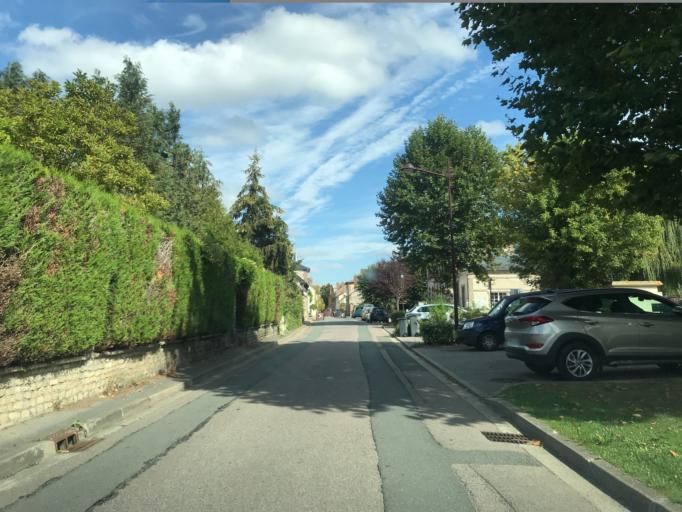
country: FR
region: Haute-Normandie
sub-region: Departement de l'Eure
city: Le Vaudreuil
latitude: 49.2549
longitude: 1.2039
